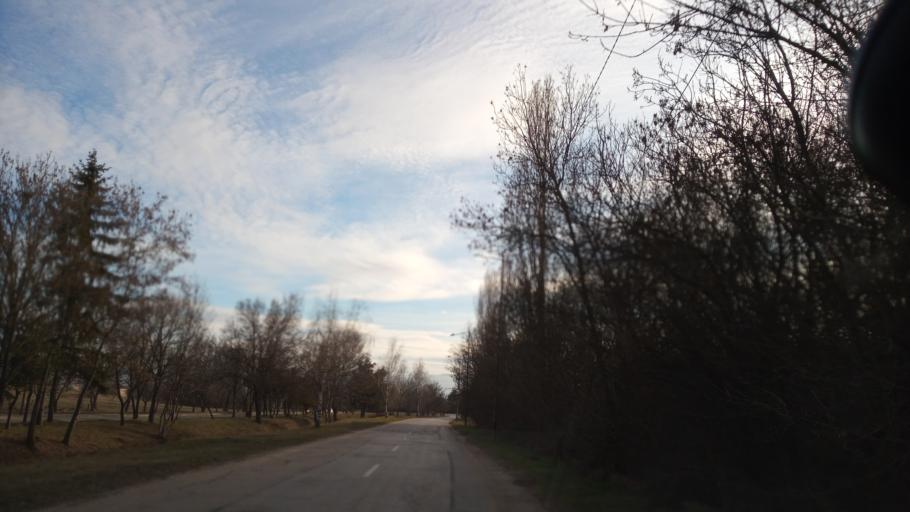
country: BG
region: Sofia-Capital
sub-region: Stolichna Obshtina
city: Bukhovo
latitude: 42.7580
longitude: 23.5604
